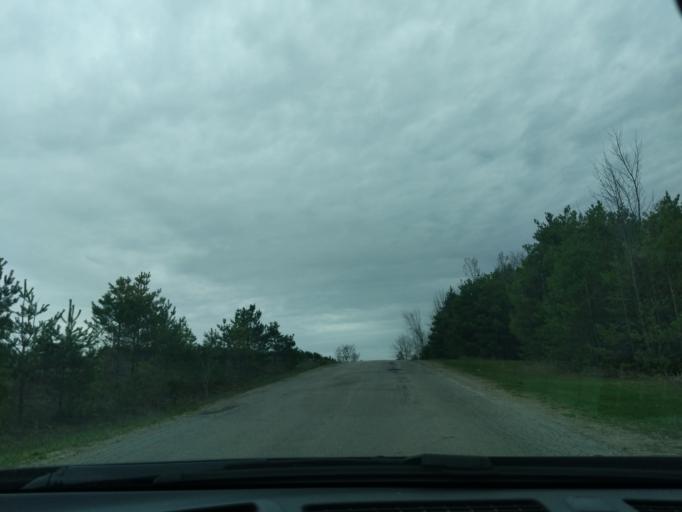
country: CA
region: Ontario
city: Orangeville
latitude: 44.0077
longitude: -79.9656
